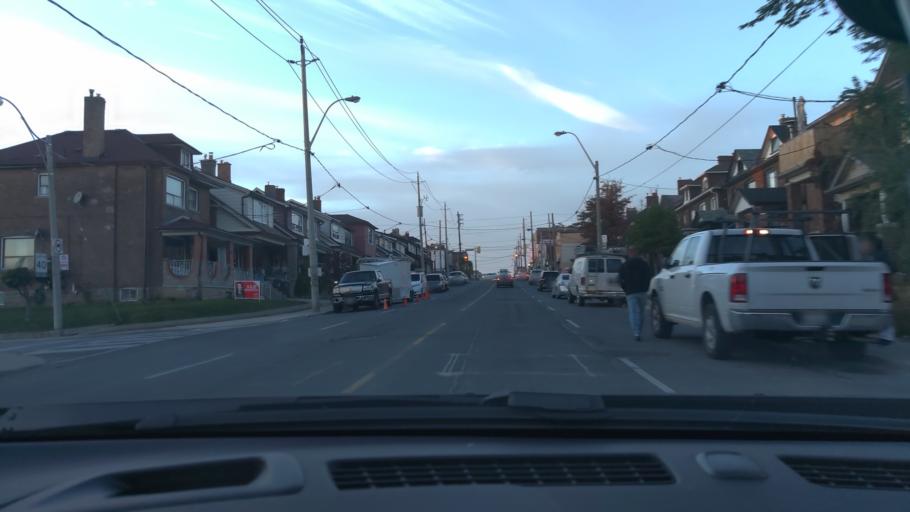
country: CA
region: Ontario
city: Toronto
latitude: 43.6843
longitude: -79.4455
